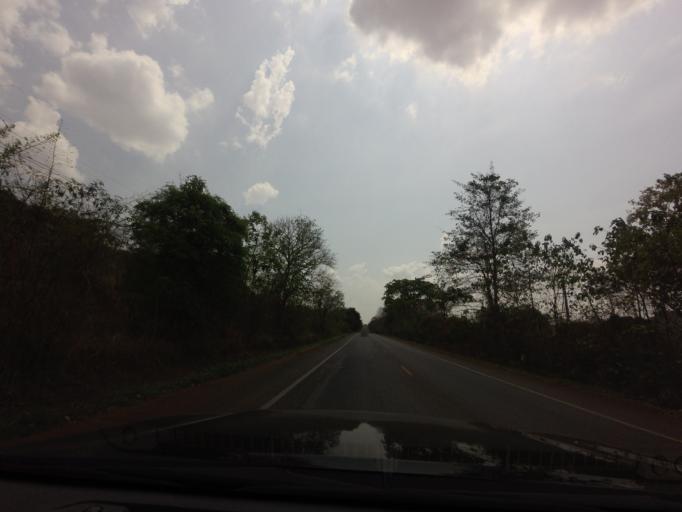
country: TH
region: Kanchanaburi
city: Sai Yok
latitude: 14.1476
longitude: 99.1445
